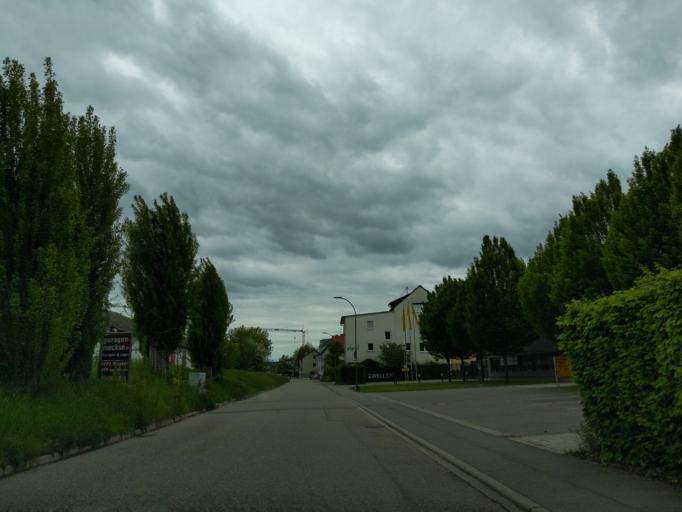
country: DE
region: Baden-Wuerttemberg
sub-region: Karlsruhe Region
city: Meckesheim
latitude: 49.3227
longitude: 8.8104
